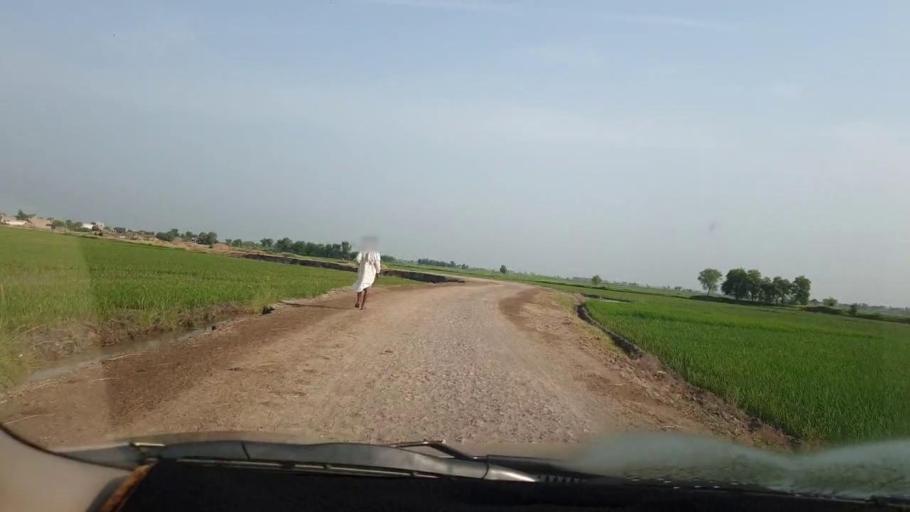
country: PK
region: Sindh
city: Goth Garelo
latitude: 27.4850
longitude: 68.0707
